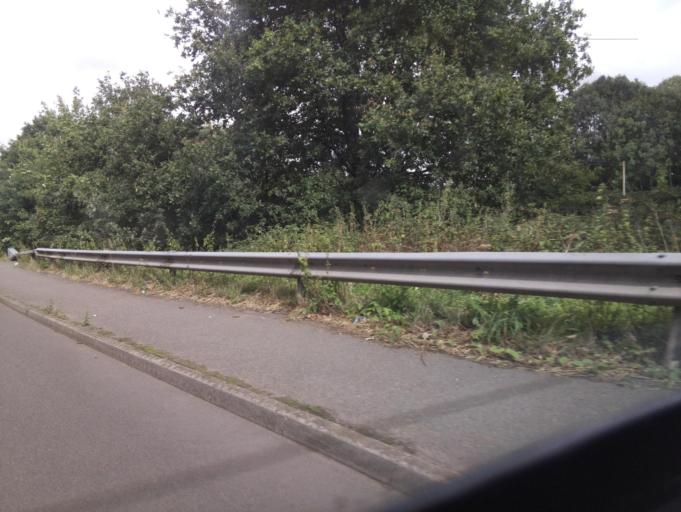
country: GB
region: England
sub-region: Telford and Wrekin
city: Newport
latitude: 52.7845
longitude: -2.3717
